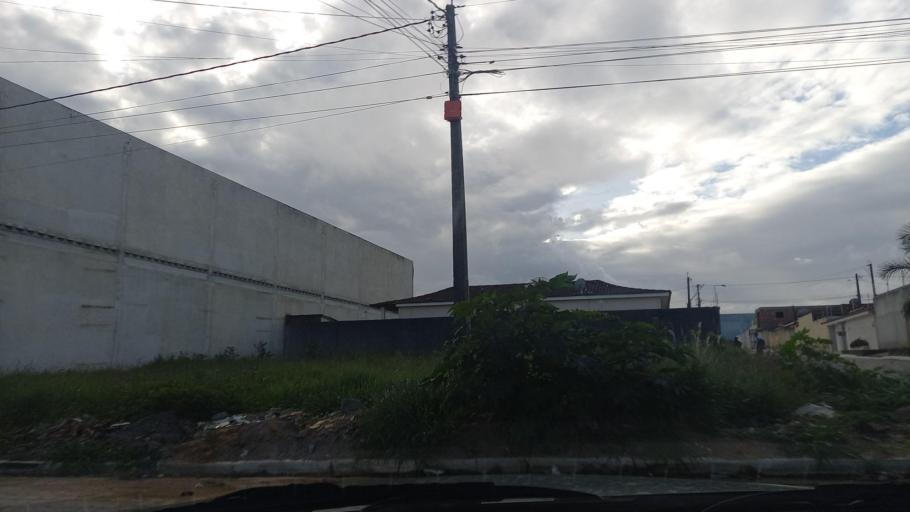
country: BR
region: Pernambuco
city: Garanhuns
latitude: -8.9100
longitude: -36.4855
